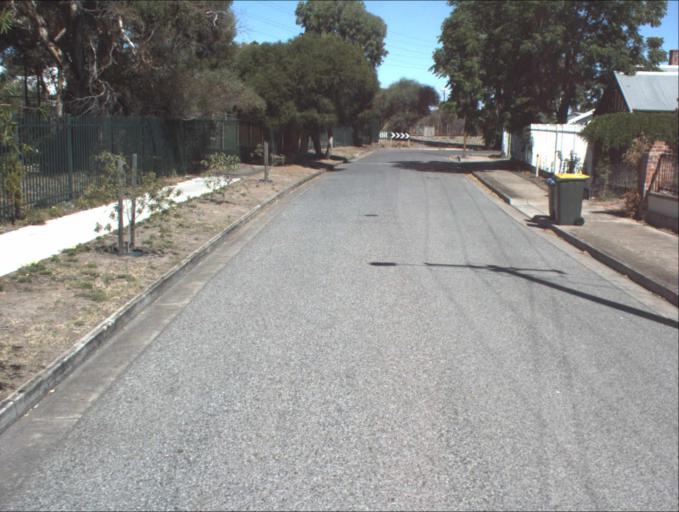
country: AU
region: South Australia
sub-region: Port Adelaide Enfield
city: Birkenhead
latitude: -34.8275
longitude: 138.4907
